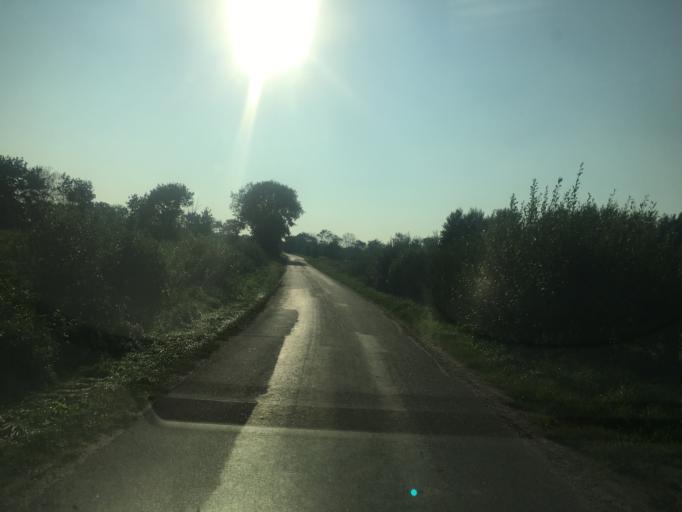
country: DE
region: Schleswig-Holstein
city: Bramstedtlund
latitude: 54.9639
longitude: 9.0594
